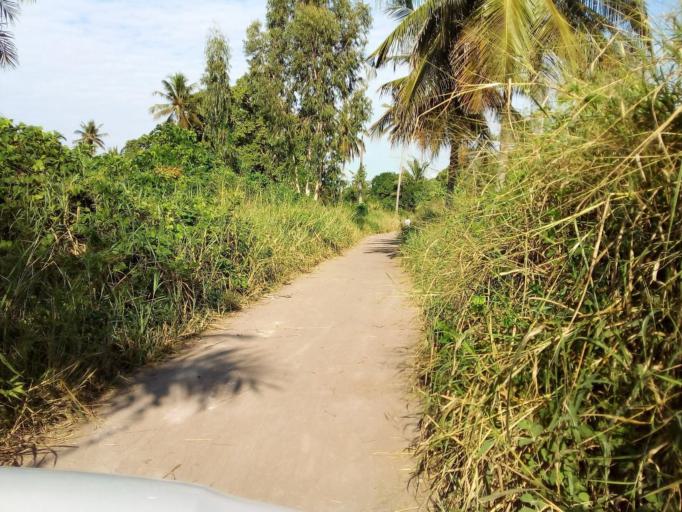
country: MZ
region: Zambezia
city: Quelimane
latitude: -17.6145
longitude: 36.8238
